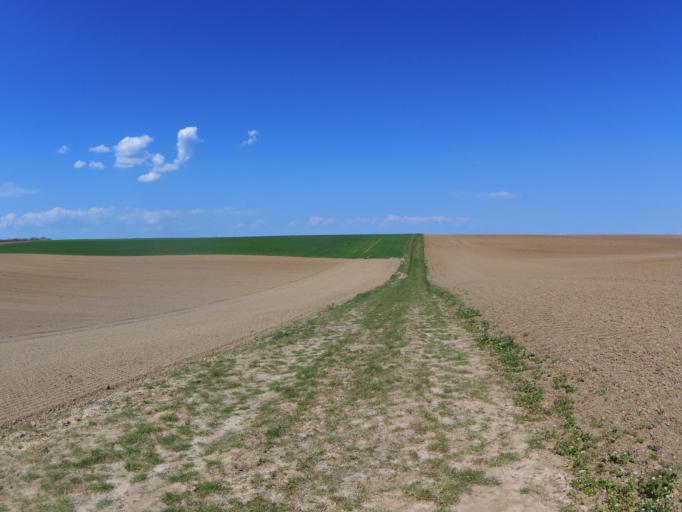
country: DE
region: Bavaria
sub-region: Regierungsbezirk Unterfranken
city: Oberpleichfeld
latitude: 49.8429
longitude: 10.0829
